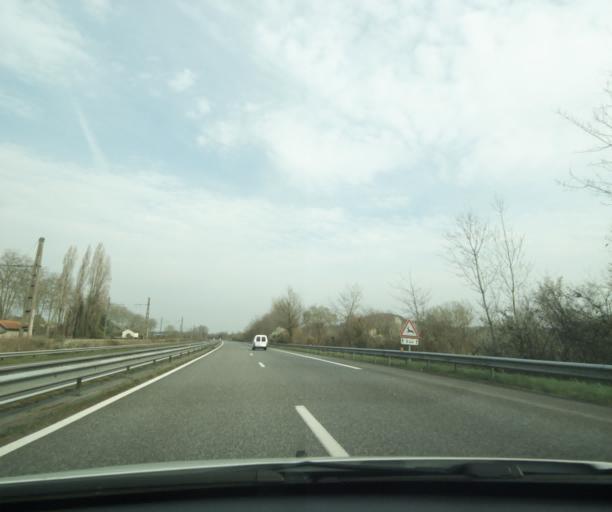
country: FR
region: Aquitaine
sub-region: Departement des Pyrenees-Atlantiques
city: Puyoo
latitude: 43.5059
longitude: -0.8661
